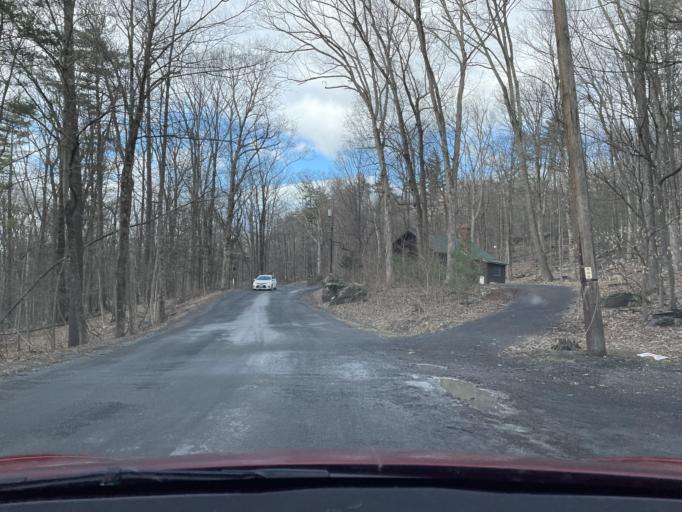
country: US
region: New York
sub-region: Ulster County
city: Woodstock
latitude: 42.0558
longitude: -74.1392
